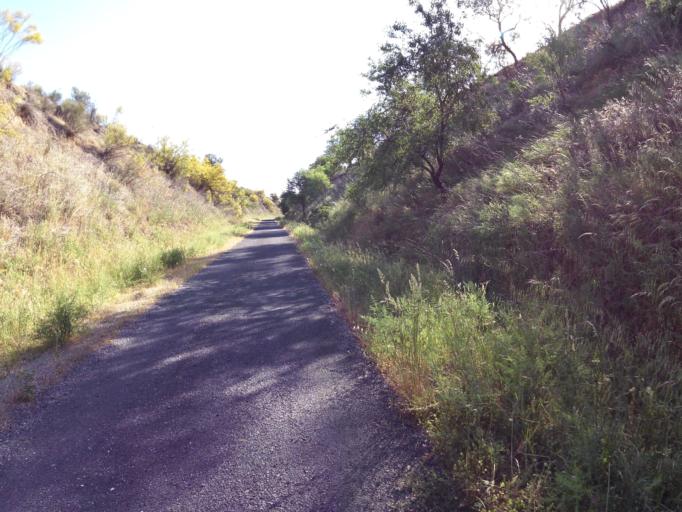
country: ES
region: Andalusia
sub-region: Province of Cordoba
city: Luque
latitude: 37.5653
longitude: -4.2400
